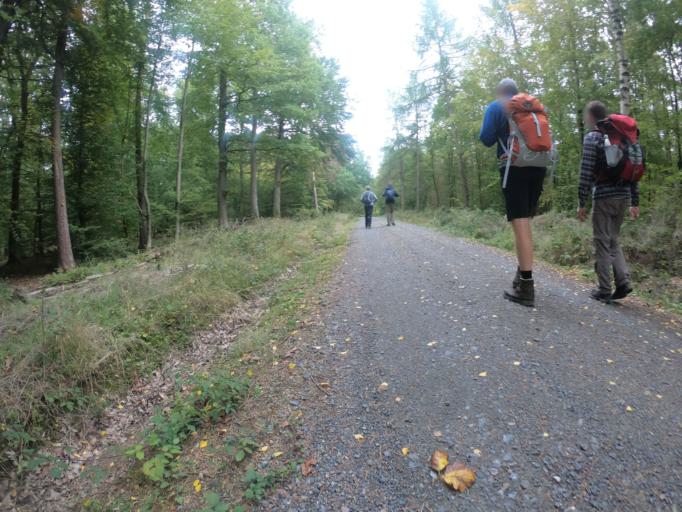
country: DE
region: Hesse
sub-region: Regierungsbezirk Darmstadt
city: Waldems
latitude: 50.2154
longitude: 8.3114
